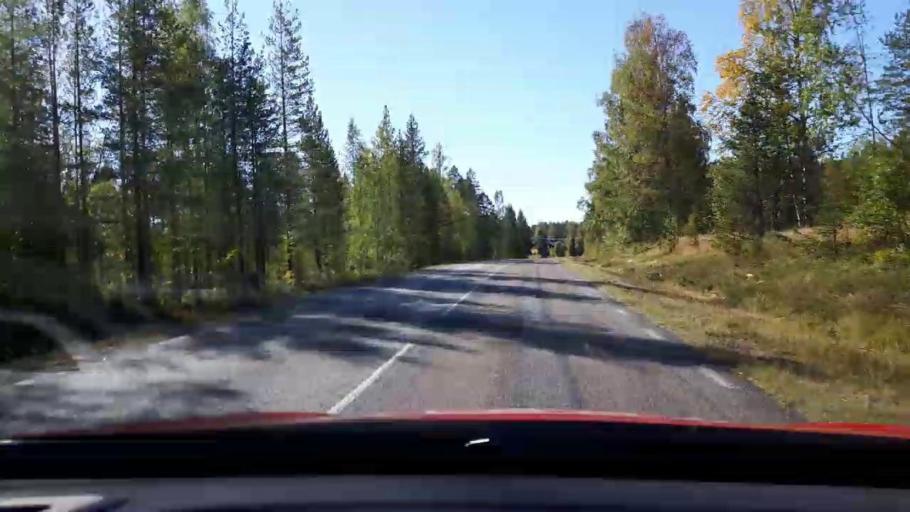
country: SE
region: Jaemtland
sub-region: Harjedalens Kommun
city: Sveg
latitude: 62.1290
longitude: 14.1653
